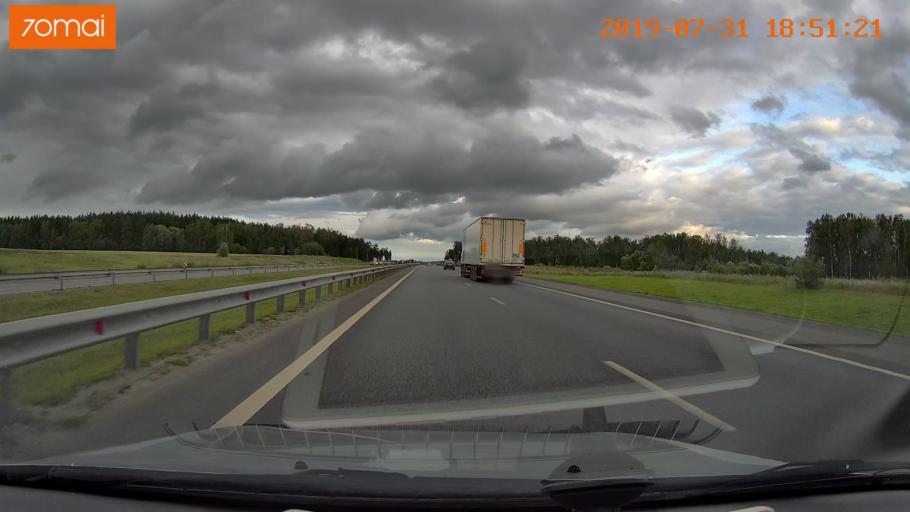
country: RU
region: Moskovskaya
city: Troitskoye
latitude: 55.2223
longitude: 38.6046
